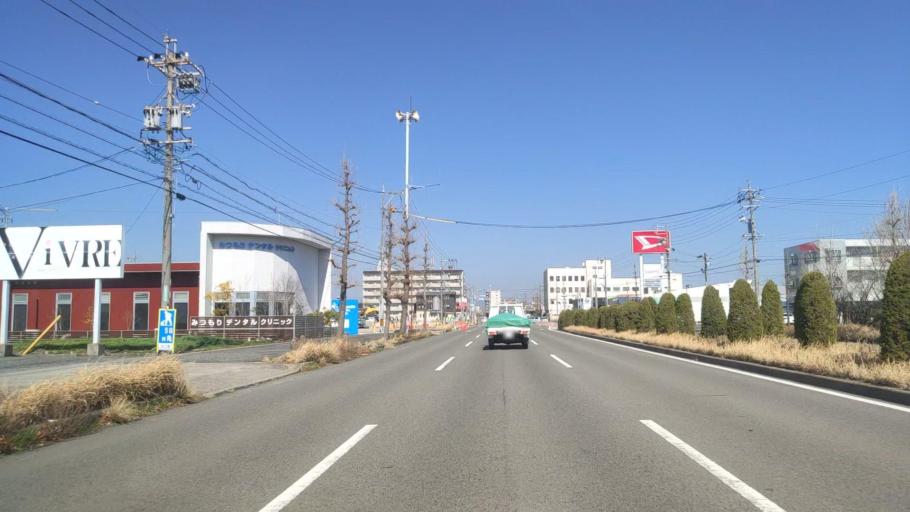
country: JP
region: Gifu
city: Kasamatsucho
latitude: 35.3908
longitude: 136.7475
